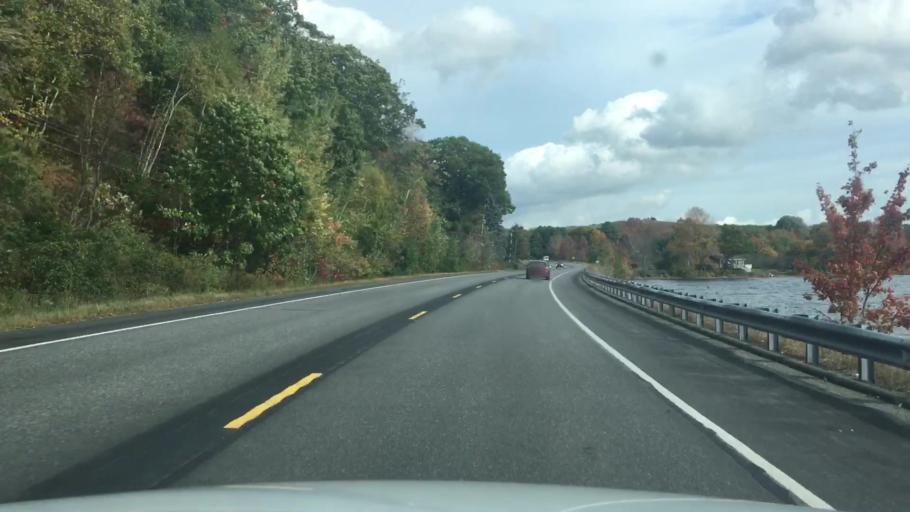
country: US
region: Maine
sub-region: Knox County
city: Rockland
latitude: 44.1471
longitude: -69.1166
